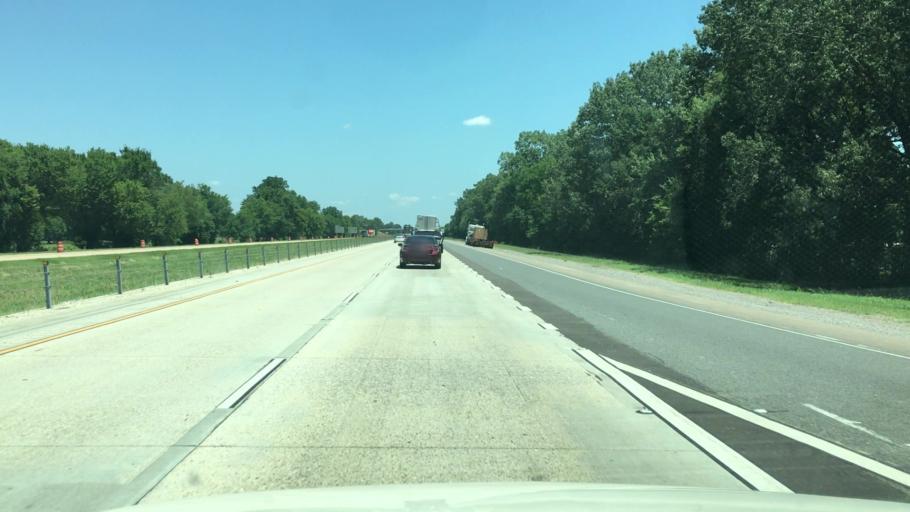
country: US
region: Arkansas
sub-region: Miller County
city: Texarkana
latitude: 33.5193
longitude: -93.9349
